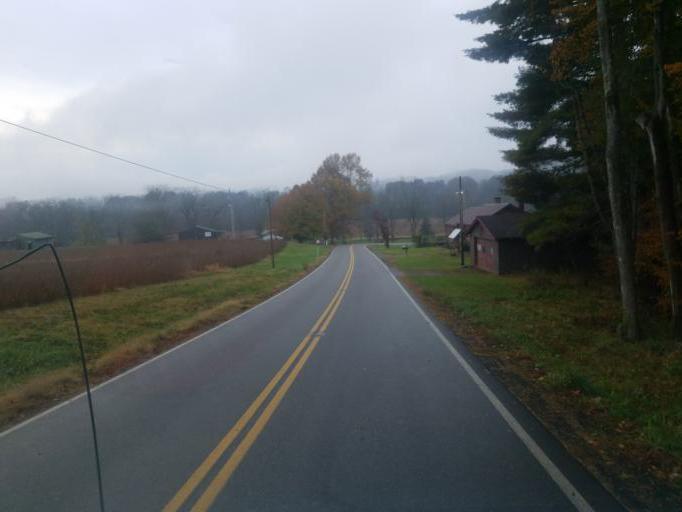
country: US
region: Ohio
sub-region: Morgan County
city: McConnelsville
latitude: 39.5577
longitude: -81.7918
